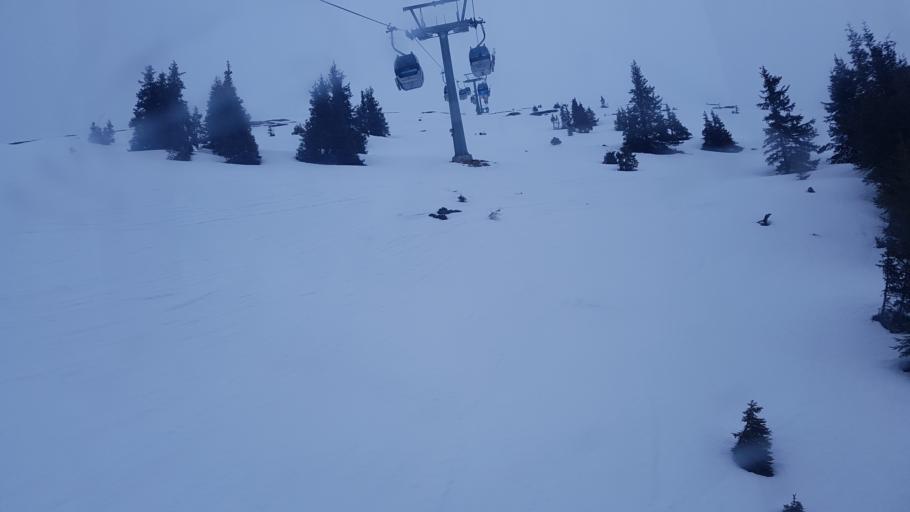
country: AT
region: Salzburg
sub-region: Politischer Bezirk Zell am See
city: Neukirchen am Grossvenediger
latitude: 47.2747
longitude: 12.2811
